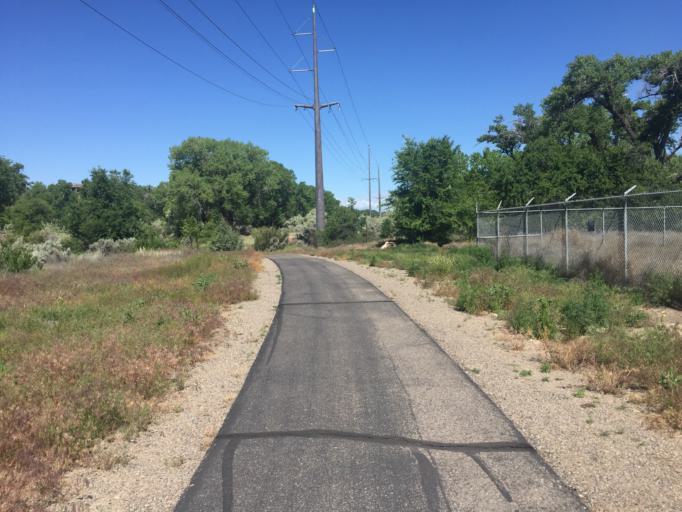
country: US
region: Colorado
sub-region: Mesa County
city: Grand Junction
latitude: 39.0682
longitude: -108.5931
